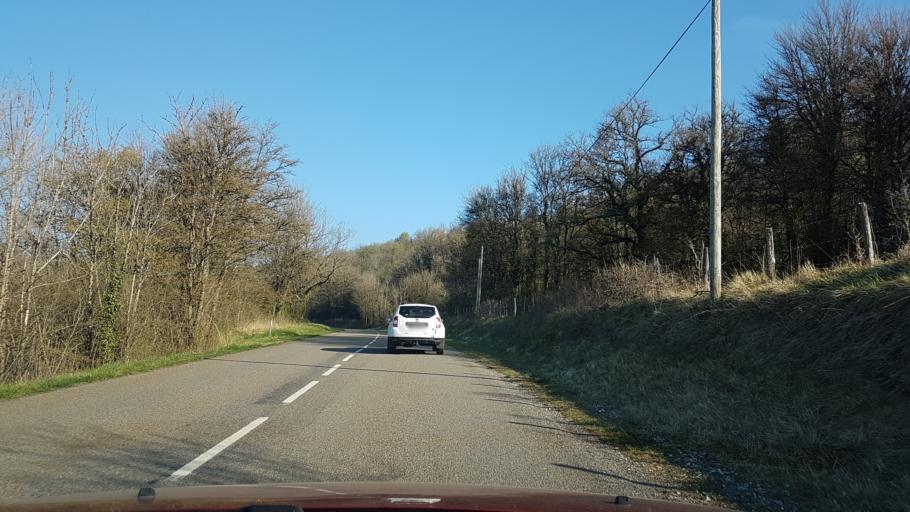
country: FR
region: Bourgogne
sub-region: Departement de Saone-et-Loire
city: Cuiseaux
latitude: 46.4546
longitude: 5.4151
